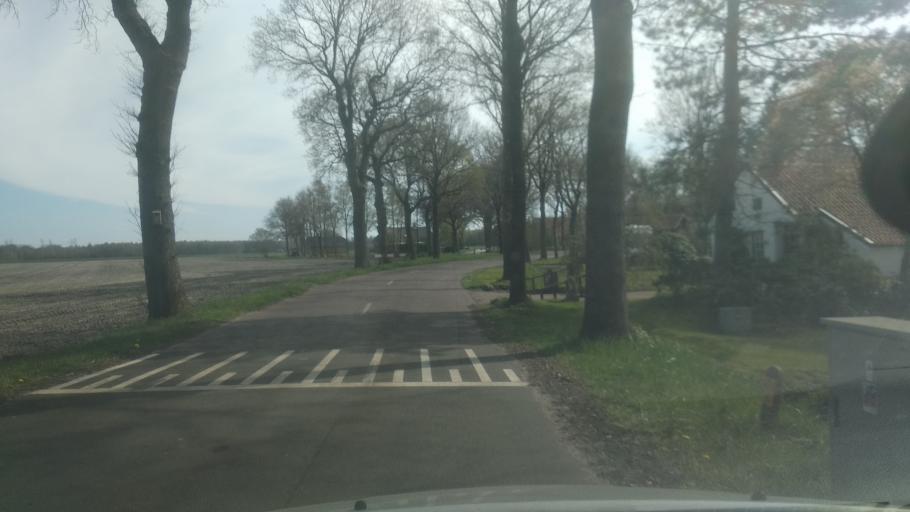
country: NL
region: Groningen
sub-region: Gemeente Stadskanaal
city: Stadskanaal
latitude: 52.9476
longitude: 6.8756
